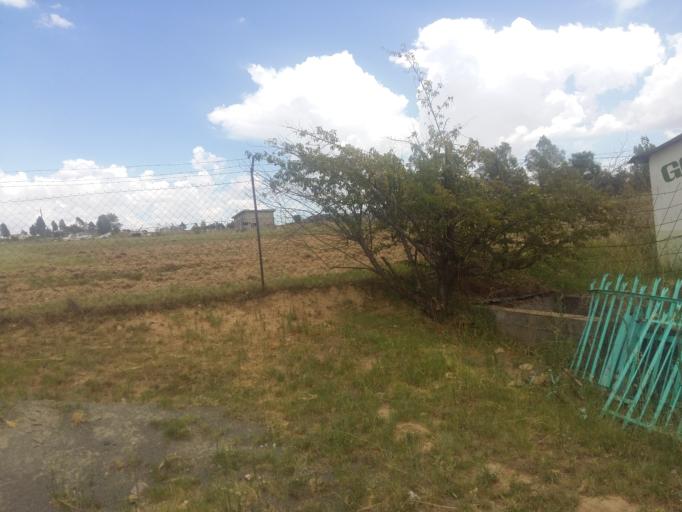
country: LS
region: Mafeteng
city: Mafeteng
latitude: -29.6900
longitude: 27.4359
